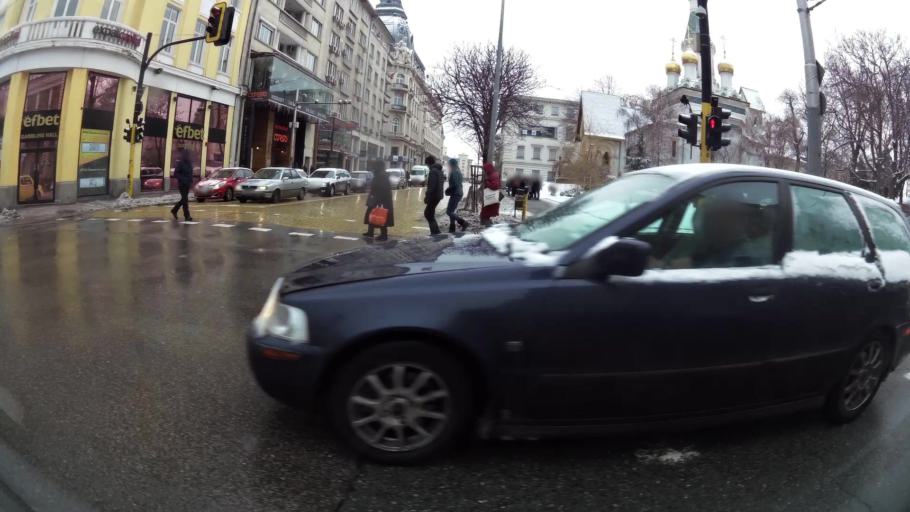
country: BG
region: Sofia-Capital
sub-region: Stolichna Obshtina
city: Sofia
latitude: 42.6952
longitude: 23.3293
